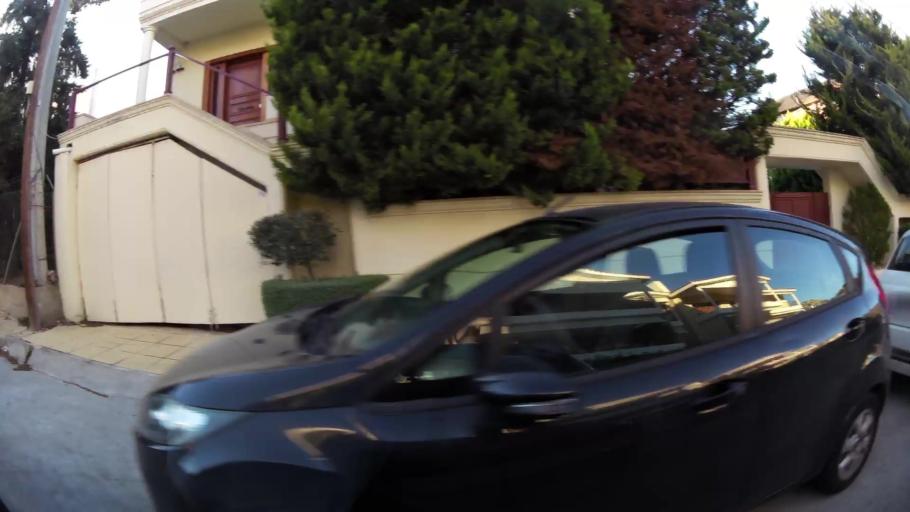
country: GR
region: Attica
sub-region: Nomarchia Anatolikis Attikis
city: Vari
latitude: 37.8276
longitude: 23.7926
